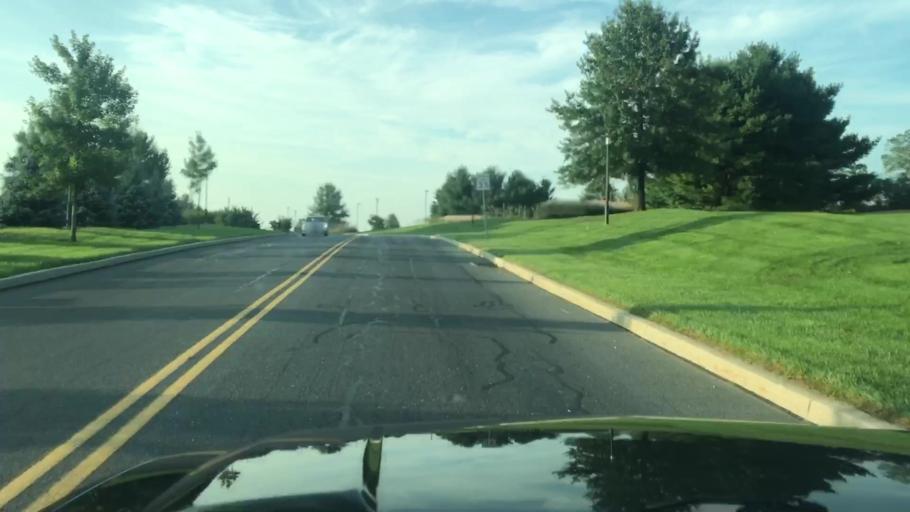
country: US
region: Pennsylvania
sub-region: Cumberland County
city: Enola
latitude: 40.2874
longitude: -76.9774
